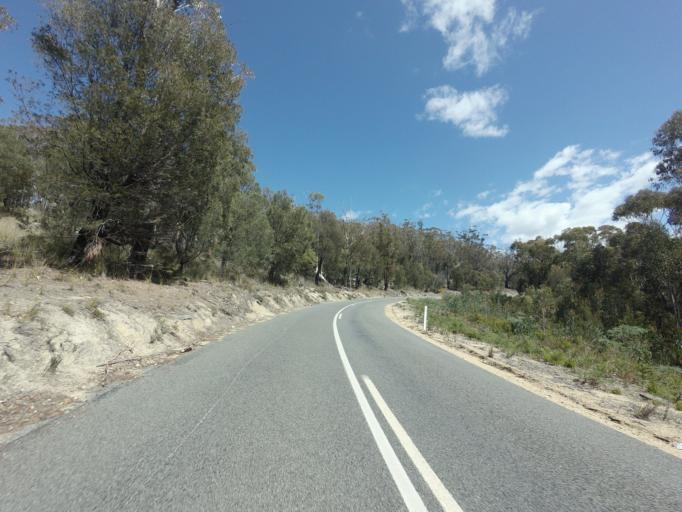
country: AU
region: Tasmania
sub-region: Break O'Day
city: St Helens
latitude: -41.6638
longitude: 148.2685
